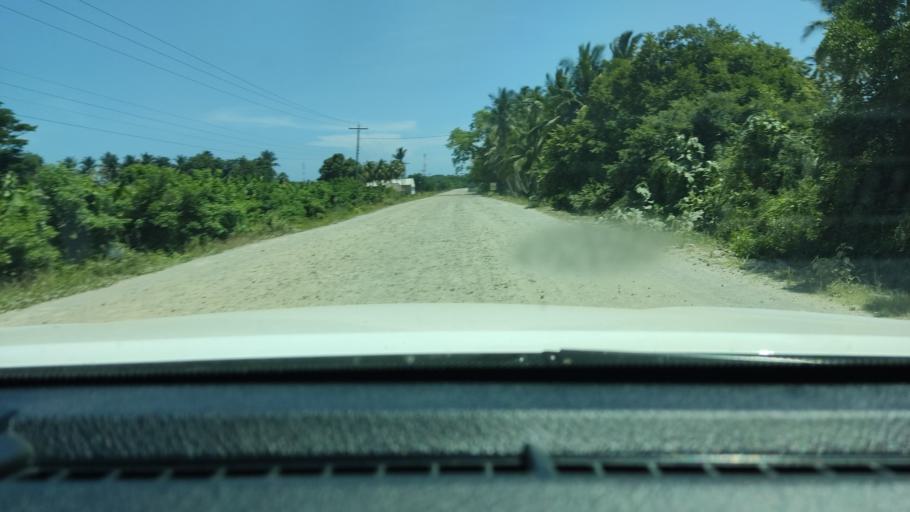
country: SV
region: Ahuachapan
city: San Francisco Menendez
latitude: 13.7621
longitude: -90.1170
